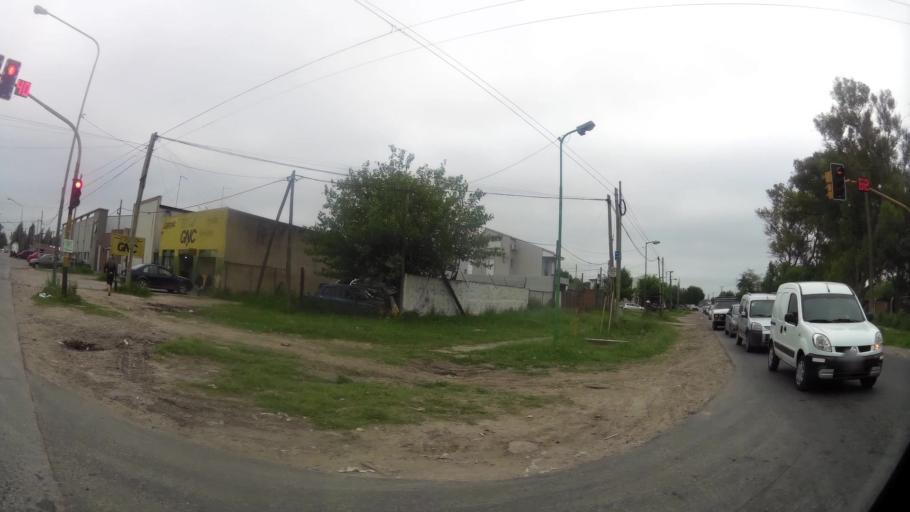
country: AR
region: Buenos Aires
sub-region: Partido de La Plata
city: La Plata
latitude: -34.9342
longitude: -57.9934
